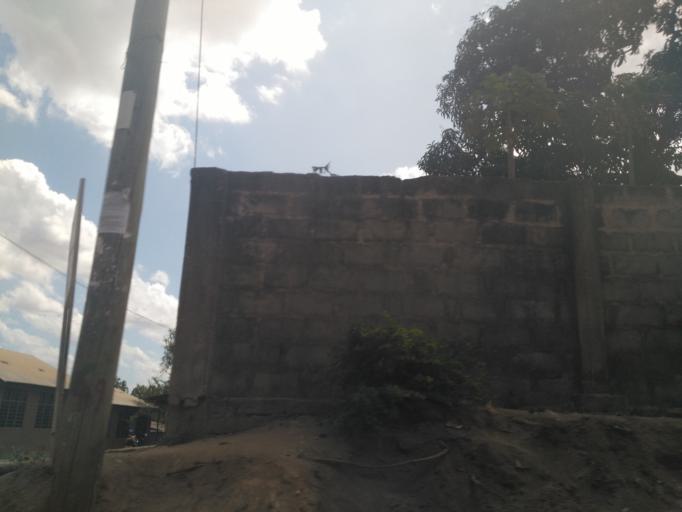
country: TZ
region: Dar es Salaam
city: Dar es Salaam
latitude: -6.8783
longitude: 39.2443
